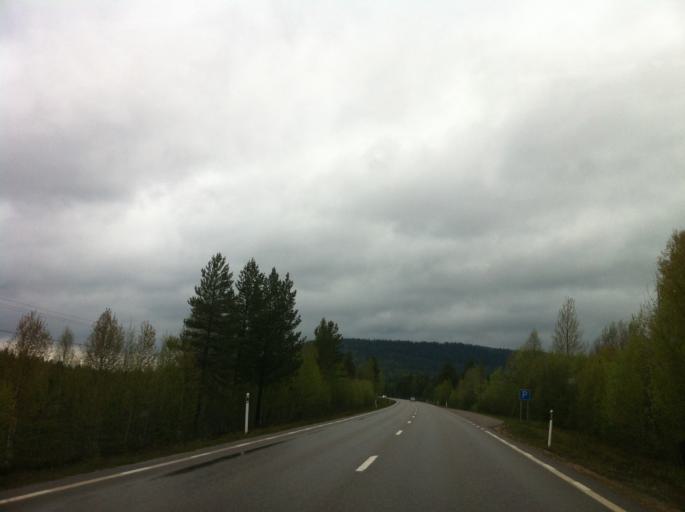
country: SE
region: Jaemtland
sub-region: Harjedalens Kommun
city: Sveg
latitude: 62.0901
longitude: 14.2463
